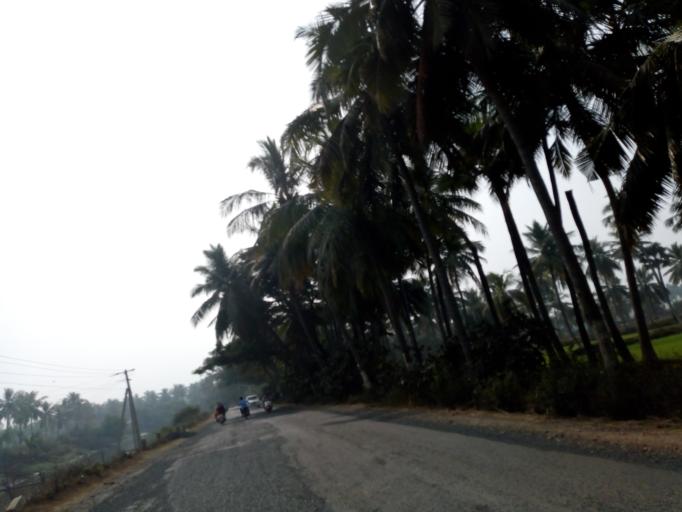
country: IN
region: Andhra Pradesh
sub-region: West Godavari
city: Akividu
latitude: 16.6149
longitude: 81.4631
